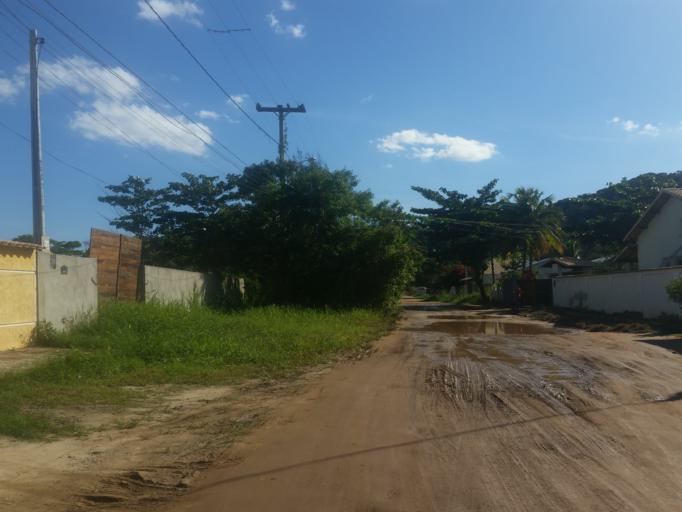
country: BR
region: Rio de Janeiro
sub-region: Marica
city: Marica
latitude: -22.9568
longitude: -42.9659
